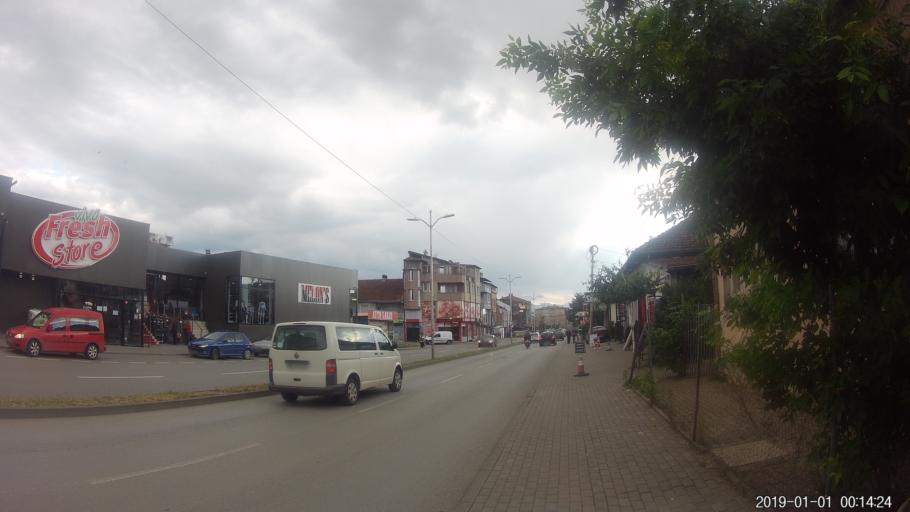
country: XK
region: Prizren
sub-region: Prizren
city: Prizren
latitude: 42.2321
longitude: 20.7615
